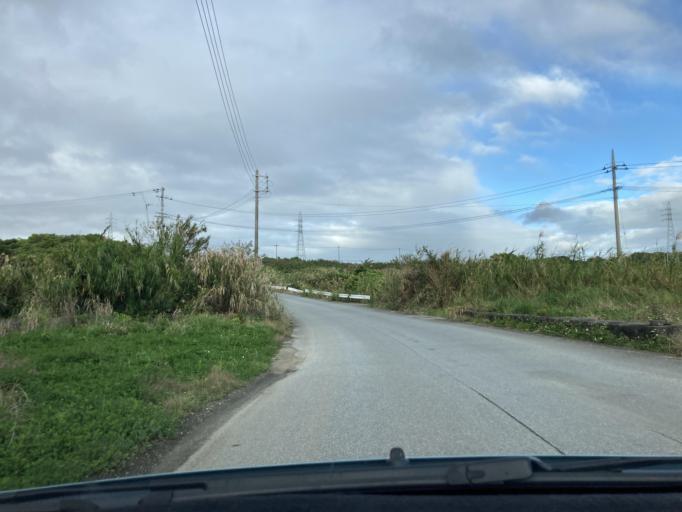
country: JP
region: Okinawa
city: Itoman
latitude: 26.1179
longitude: 127.6844
